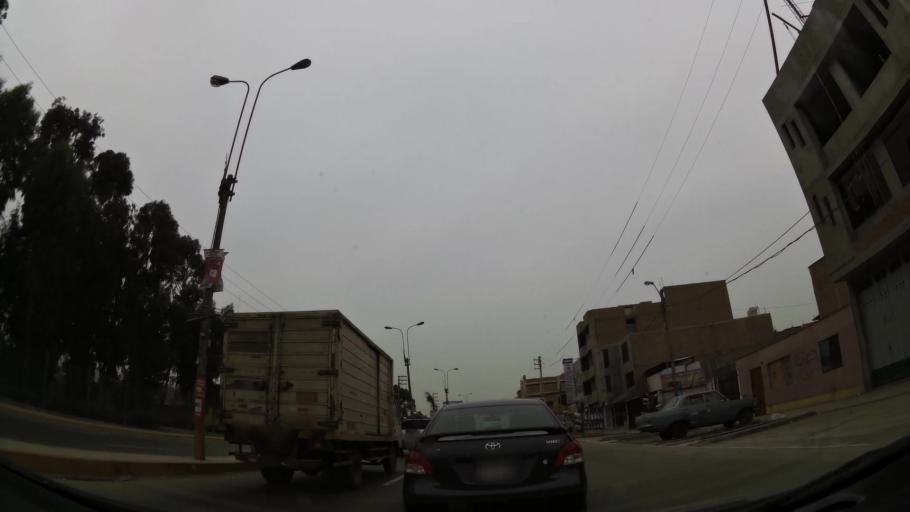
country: PE
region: Lima
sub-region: Lima
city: Surco
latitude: -12.1930
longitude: -76.9687
